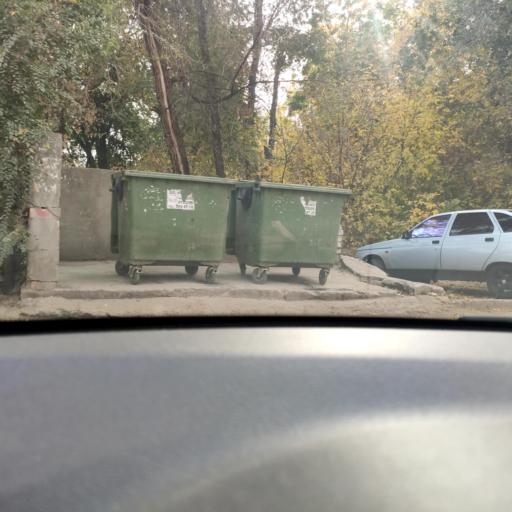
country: RU
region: Samara
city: Samara
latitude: 53.2182
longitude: 50.2085
